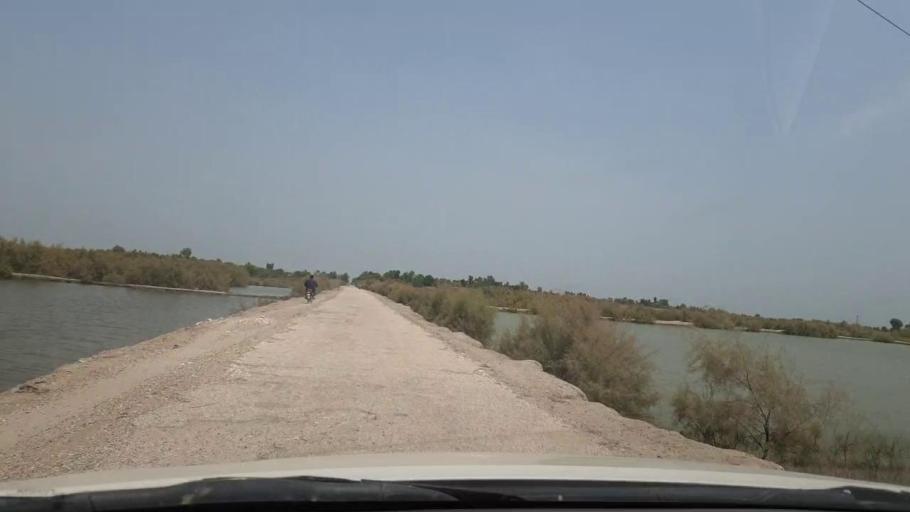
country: PK
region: Sindh
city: Rustam jo Goth
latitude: 28.0277
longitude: 68.8131
